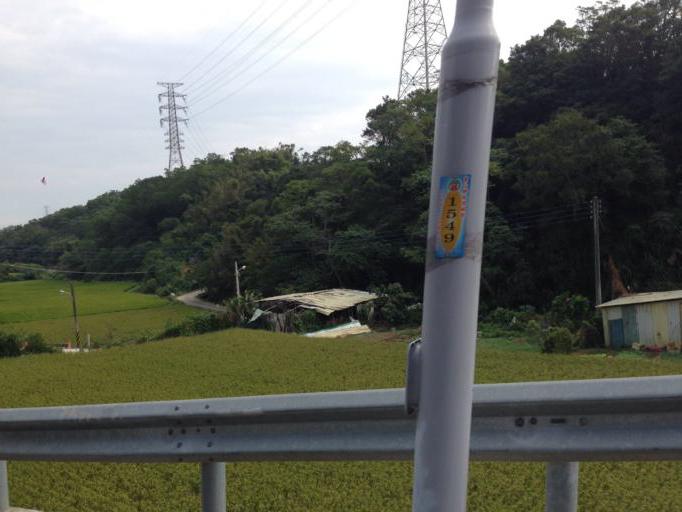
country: TW
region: Taiwan
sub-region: Hsinchu
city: Hsinchu
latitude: 24.7514
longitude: 120.9690
